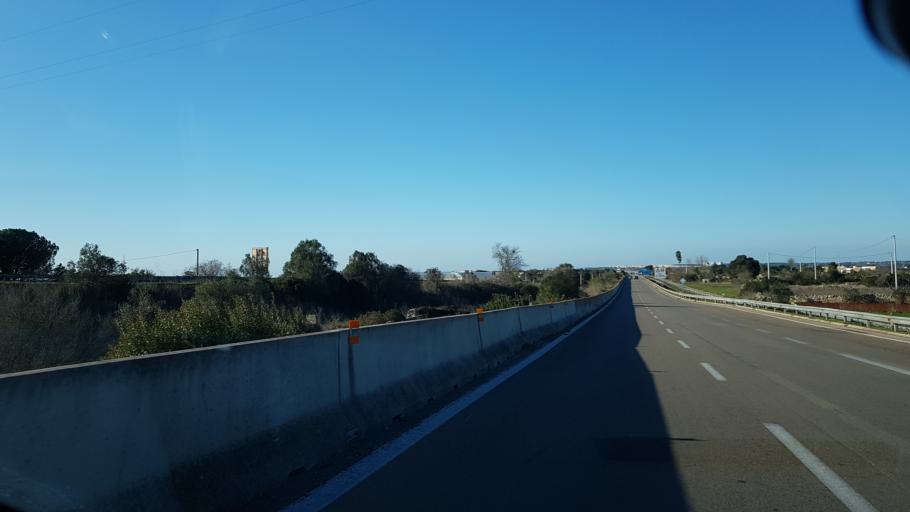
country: IT
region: Apulia
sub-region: Provincia di Lecce
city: Taviano
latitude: 40.0026
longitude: 18.0616
